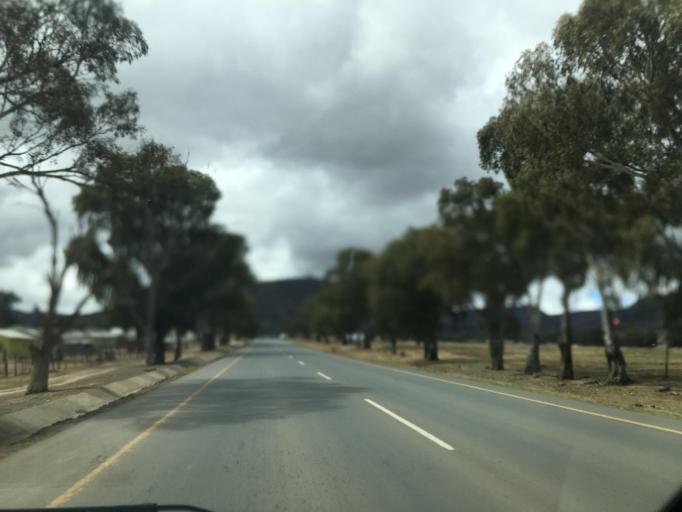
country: ZA
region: Eastern Cape
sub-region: Chris Hani District Municipality
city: Cala
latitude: -31.5287
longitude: 27.6840
